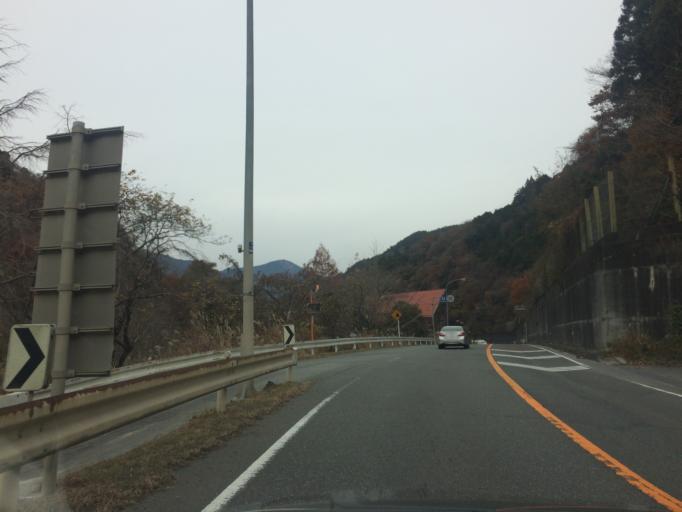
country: JP
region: Shizuoka
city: Fujinomiya
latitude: 35.3259
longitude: 138.4283
